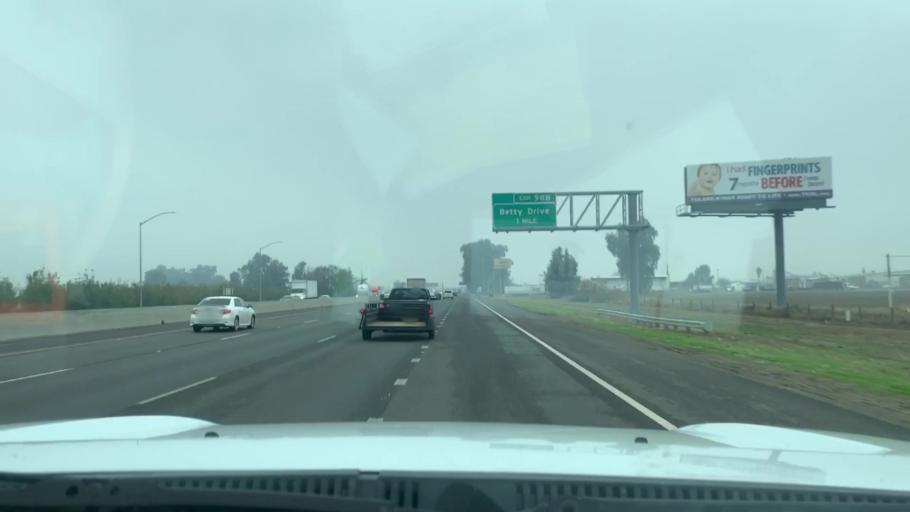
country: US
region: California
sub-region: Tulare County
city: Goshen
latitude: 36.3348
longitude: -119.4139
